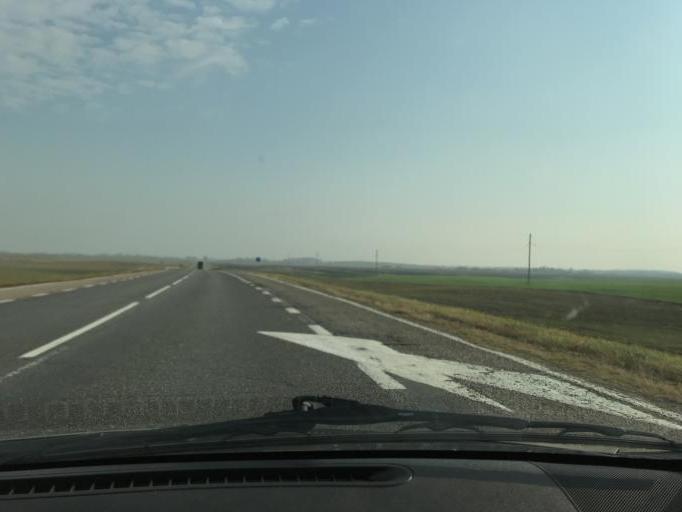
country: BY
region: Vitebsk
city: Chashniki
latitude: 55.0128
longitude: 29.0682
